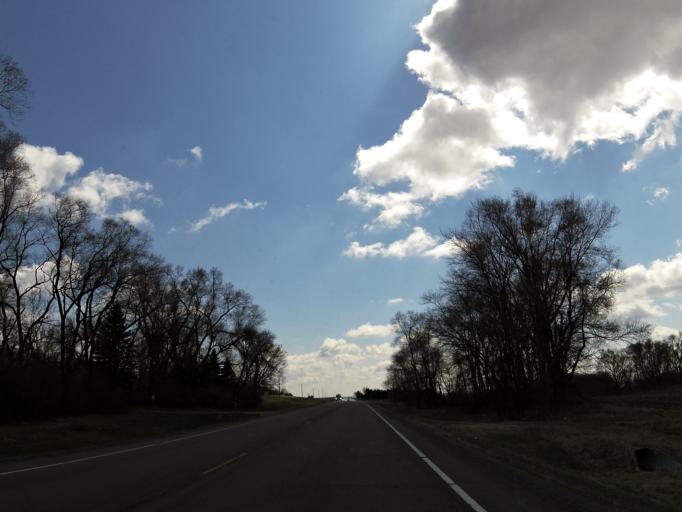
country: US
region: Minnesota
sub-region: Goodhue County
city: Cannon Falls
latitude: 44.5819
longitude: -92.9951
